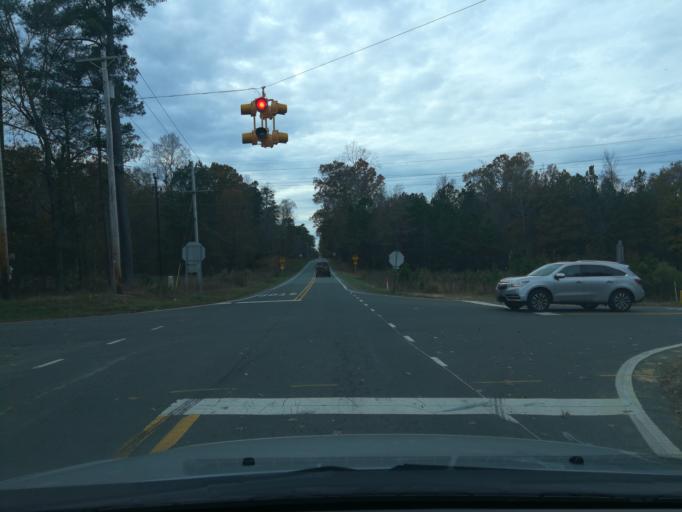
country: US
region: North Carolina
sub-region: Orange County
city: Hillsborough
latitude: 36.0315
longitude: -79.0217
